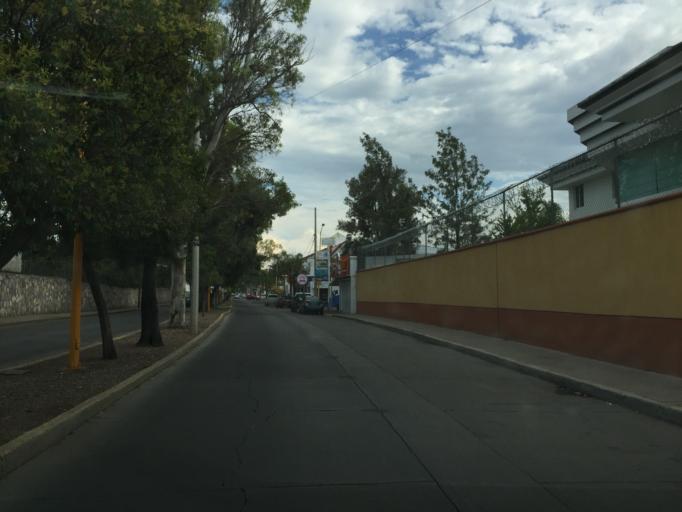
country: MX
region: Aguascalientes
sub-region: Aguascalientes
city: Pocitos
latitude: 21.9191
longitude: -102.3042
